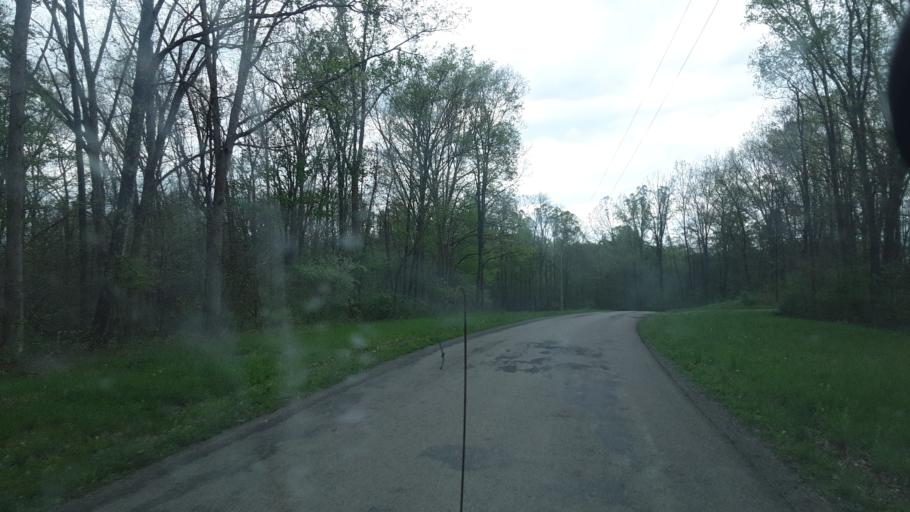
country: US
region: Ohio
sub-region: Noble County
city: Caldwell
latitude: 39.7344
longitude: -81.6809
